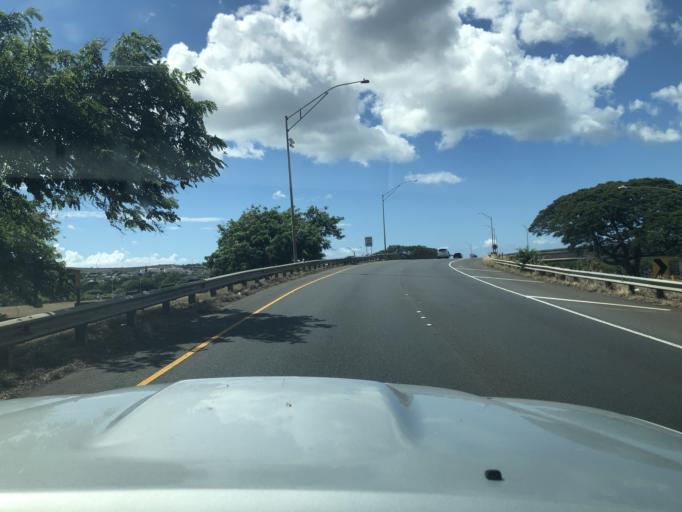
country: US
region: Hawaii
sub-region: Honolulu County
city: Halawa
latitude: 21.3752
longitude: -157.9266
